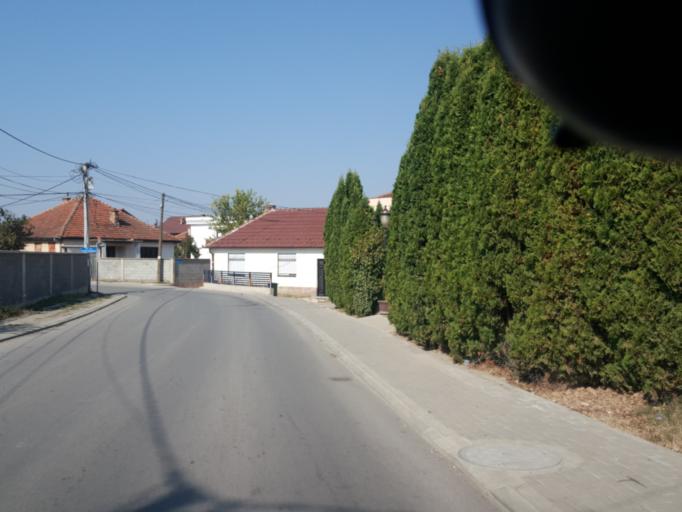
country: XK
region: Gjakova
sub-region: Komuna e Gjakoves
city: Gjakove
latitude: 42.3935
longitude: 20.4293
